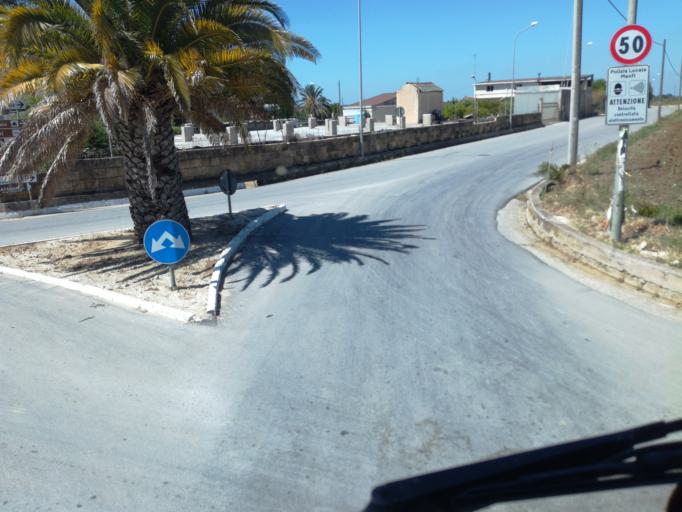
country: IT
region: Sicily
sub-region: Agrigento
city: Menfi
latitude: 37.6143
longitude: 12.9725
